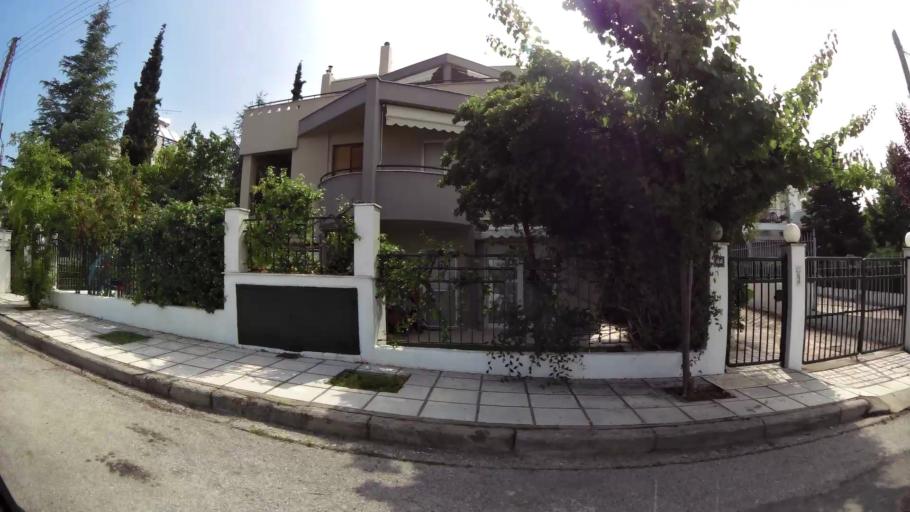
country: GR
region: Central Macedonia
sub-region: Nomos Thessalonikis
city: Panorama
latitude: 40.5813
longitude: 23.0130
